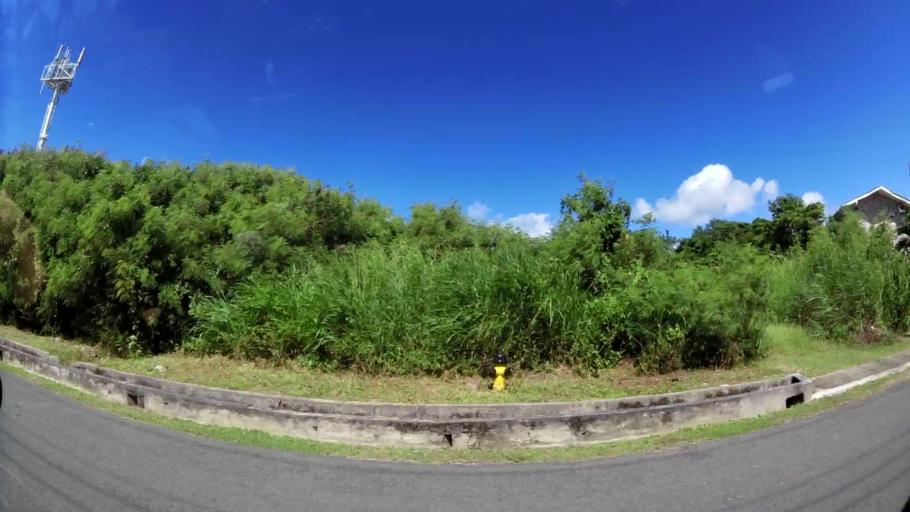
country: TT
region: Tobago
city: Scarborough
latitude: 11.1567
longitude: -60.7735
